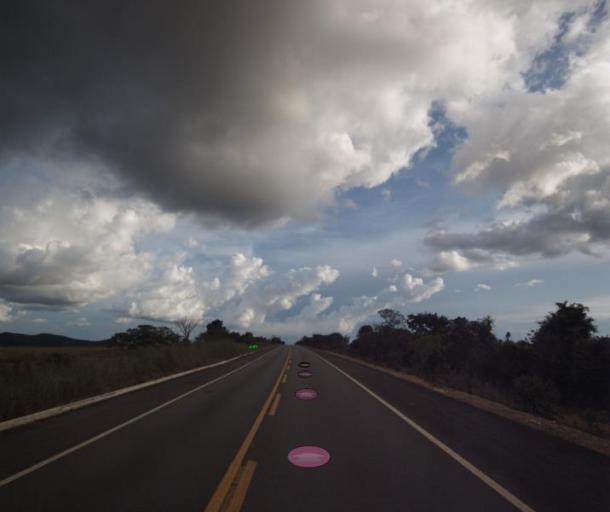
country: BR
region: Goias
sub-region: Niquelandia
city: Niquelandia
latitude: -14.7013
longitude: -48.6025
